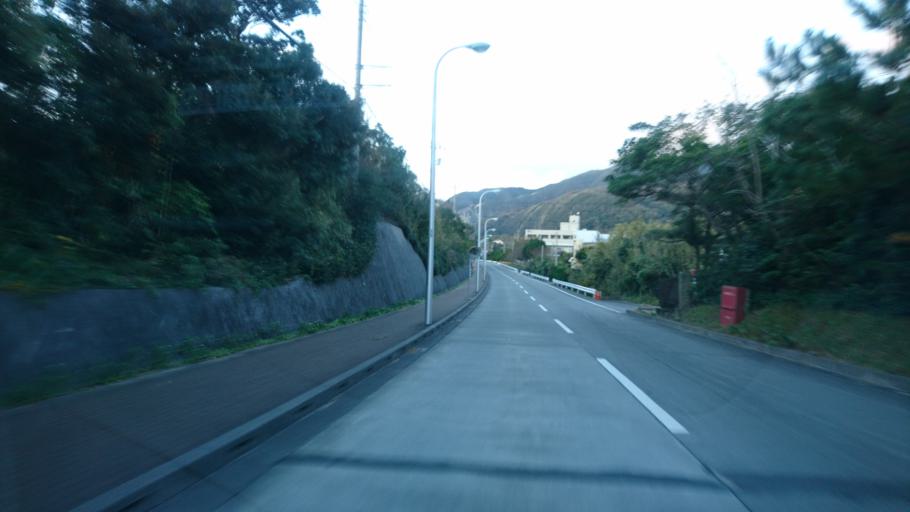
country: JP
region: Shizuoka
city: Shimoda
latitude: 34.3695
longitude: 139.2592
